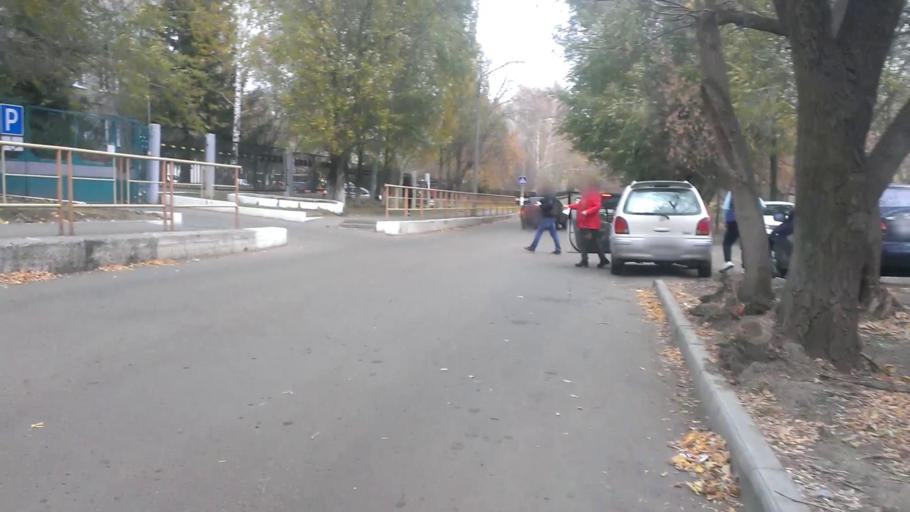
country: RU
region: Altai Krai
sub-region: Gorod Barnaulskiy
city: Barnaul
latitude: 53.3658
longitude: 83.7180
